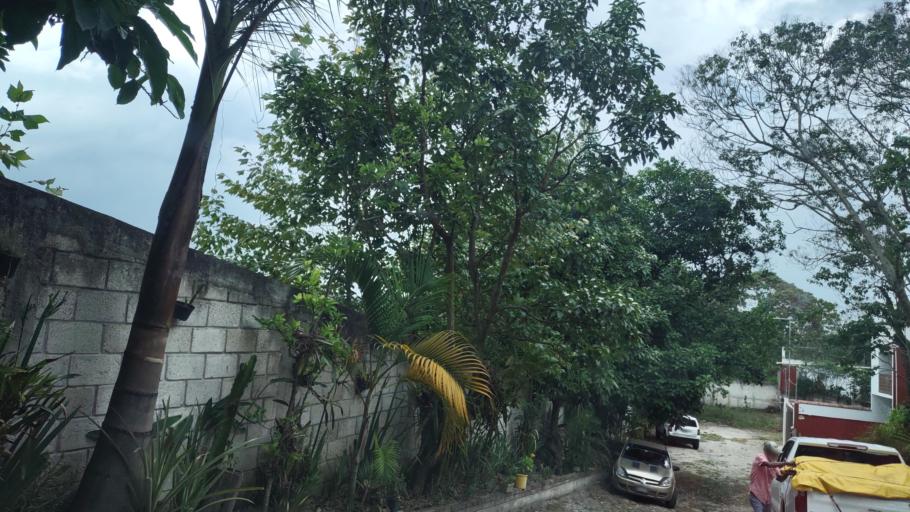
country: MX
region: Veracruz
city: Coatepec
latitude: 19.4606
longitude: -96.9480
